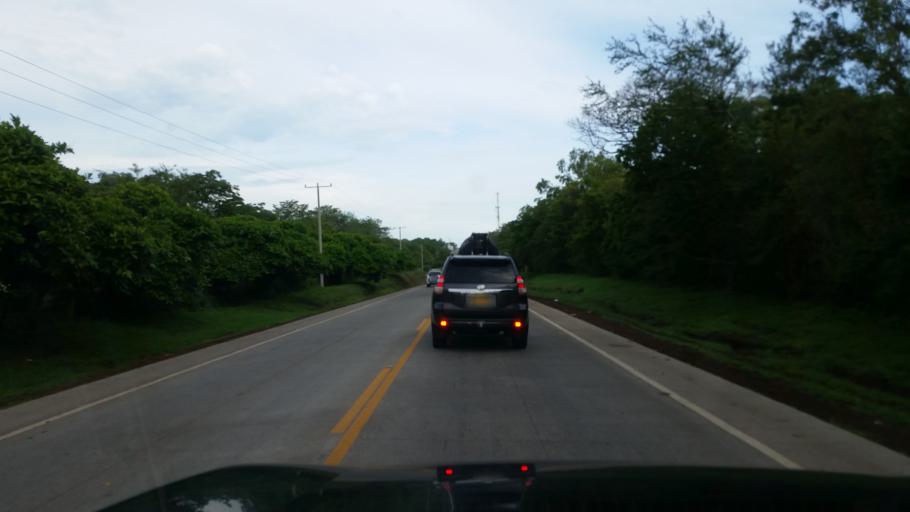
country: NI
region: Managua
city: Carlos Fonseca Amador
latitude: 12.0713
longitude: -86.4902
